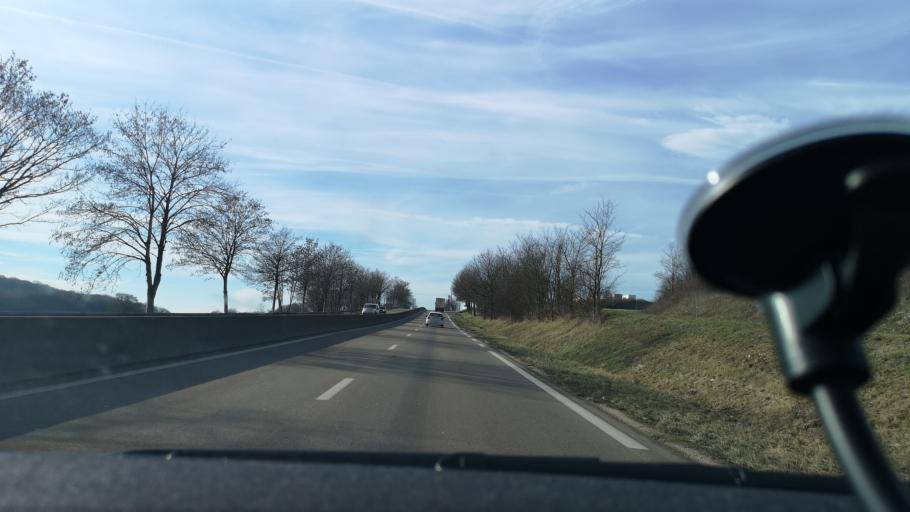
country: FR
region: Franche-Comte
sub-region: Departement du Doubs
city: Grandfontaine
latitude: 47.2049
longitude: 5.8898
